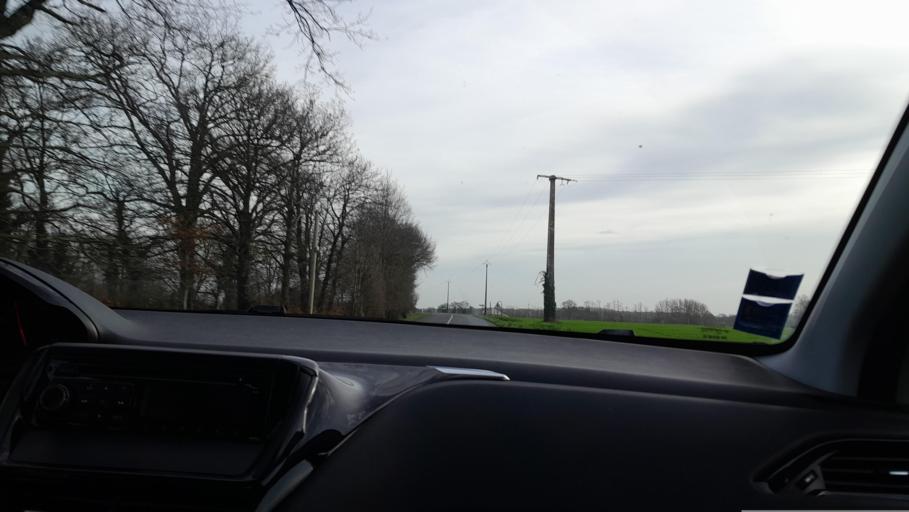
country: FR
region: Brittany
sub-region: Departement d'Ille-et-Vilaine
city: La Guerche-de-Bretagne
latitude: 47.9510
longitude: -1.1910
